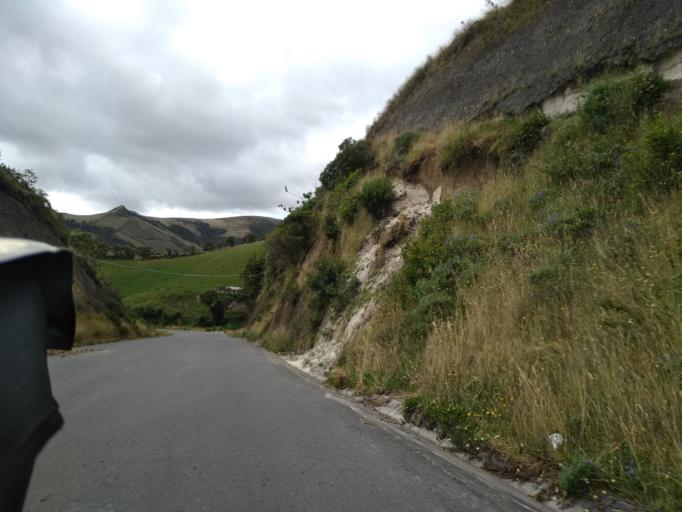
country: EC
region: Cotopaxi
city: Saquisili
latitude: -0.7283
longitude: -78.7533
